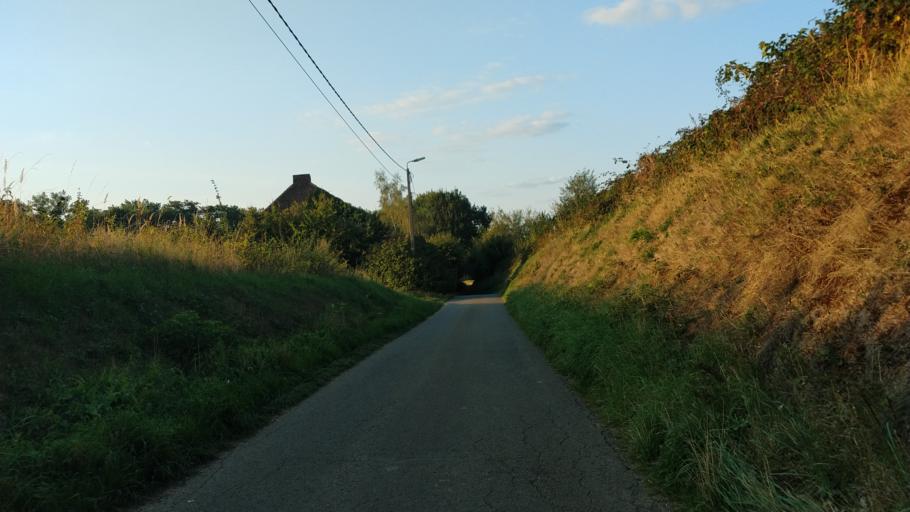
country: BE
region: Flanders
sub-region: Provincie Vlaams-Brabant
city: Holsbeek
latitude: 50.8842
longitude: 4.7831
